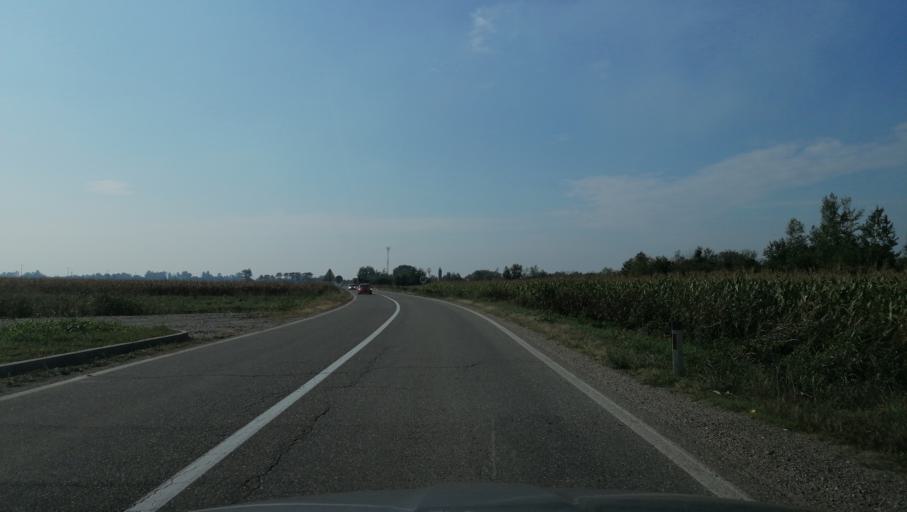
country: BA
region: Republika Srpska
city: Popovi
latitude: 44.7807
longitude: 19.3081
